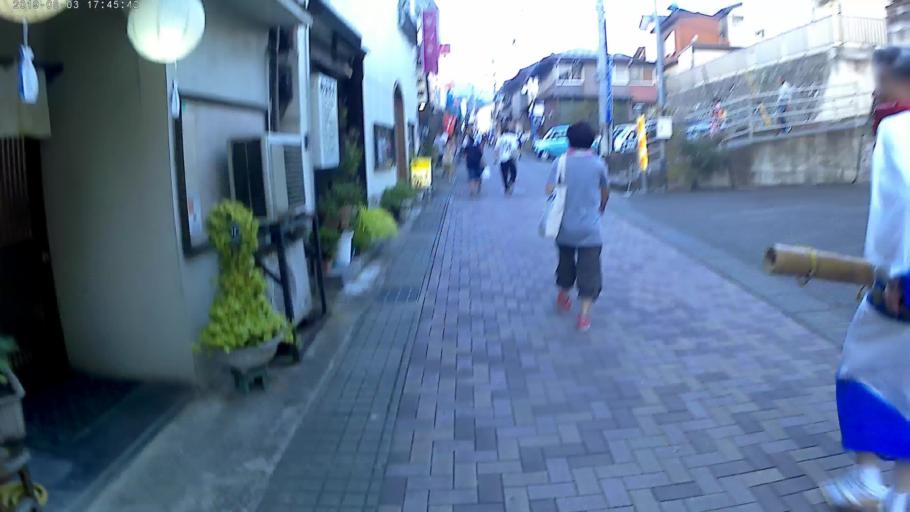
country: JP
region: Yamanashi
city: Otsuki
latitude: 35.6132
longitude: 138.9436
